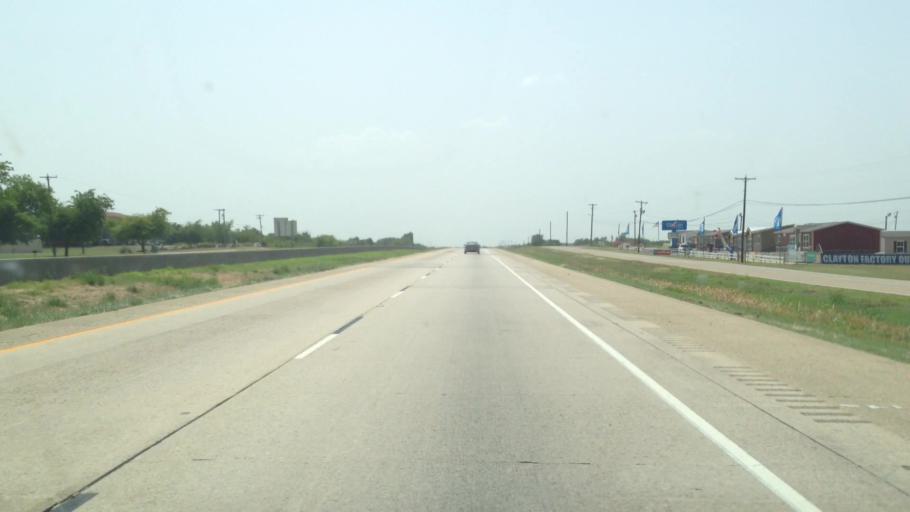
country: US
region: Texas
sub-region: Hopkins County
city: Sulphur Springs
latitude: 33.1210
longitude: -95.6533
